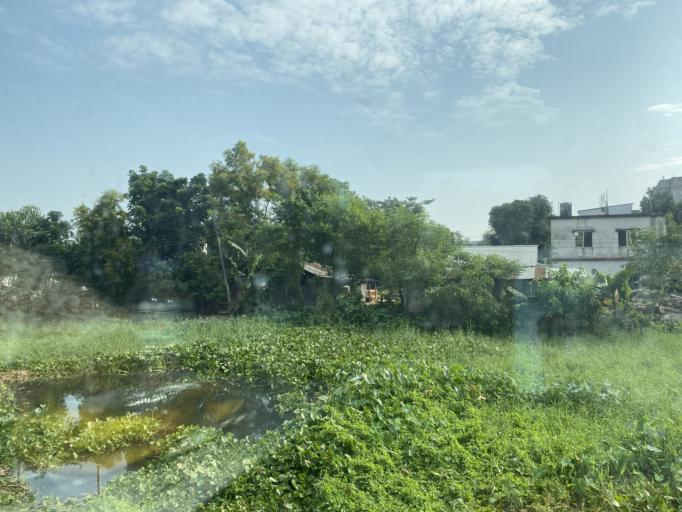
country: BD
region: Chittagong
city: Nabinagar
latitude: 23.9505
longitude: 91.1200
